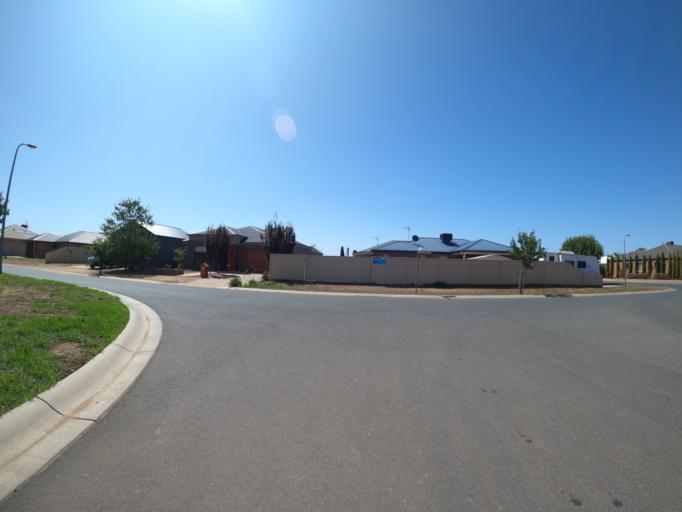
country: AU
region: Victoria
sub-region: Moira
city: Yarrawonga
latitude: -36.0107
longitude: 146.0253
